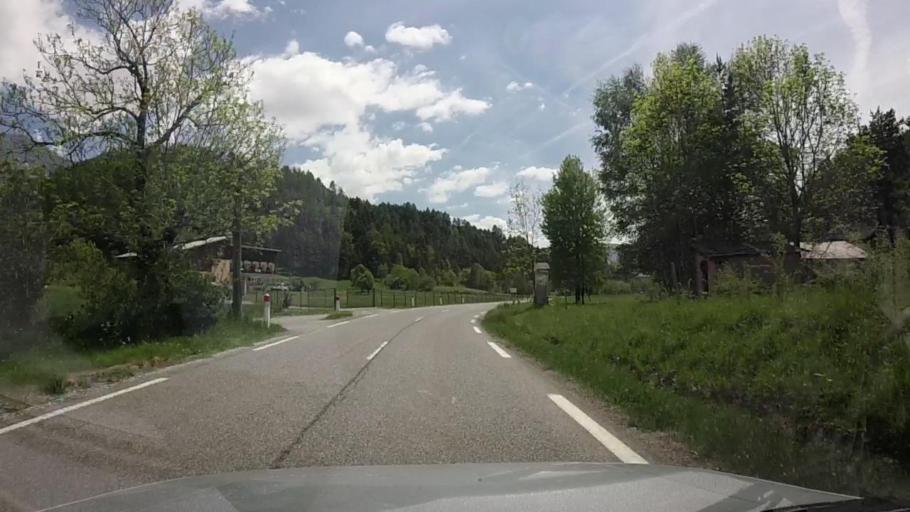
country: FR
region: Provence-Alpes-Cote d'Azur
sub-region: Departement des Alpes-de-Haute-Provence
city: Seyne-les-Alpes
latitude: 44.3193
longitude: 6.4021
